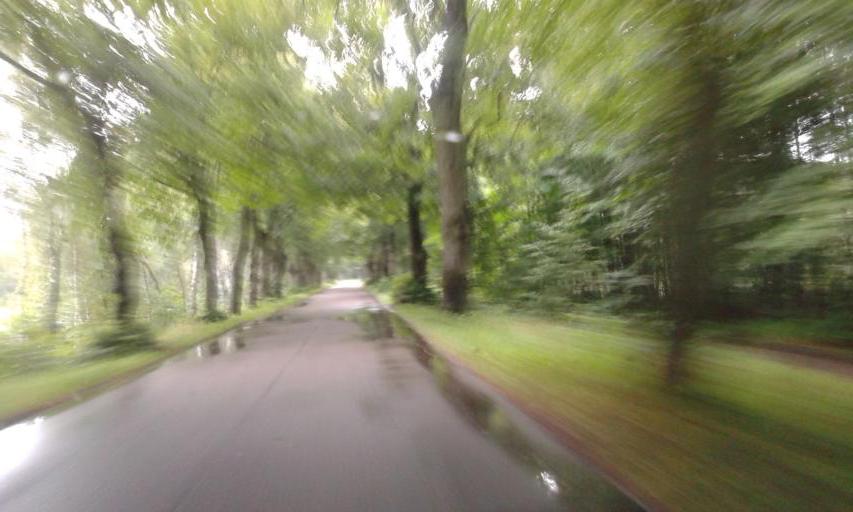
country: PL
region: West Pomeranian Voivodeship
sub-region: Powiat szczecinecki
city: Borne Sulinowo
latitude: 53.4977
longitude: 16.5003
